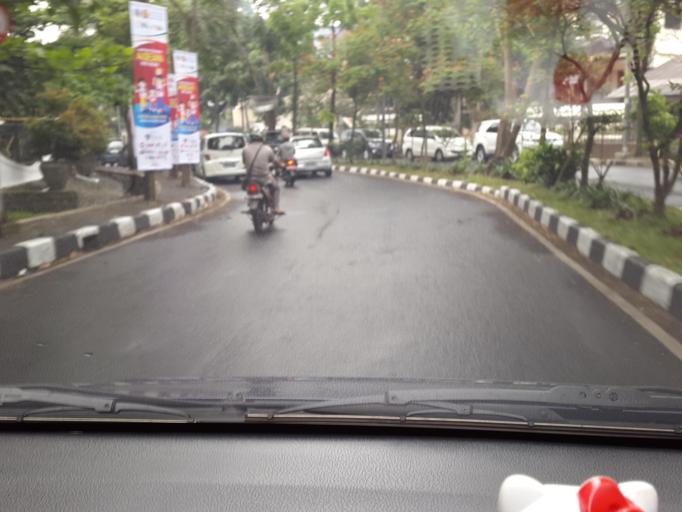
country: ID
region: West Java
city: Bandung
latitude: -6.9035
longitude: 107.6174
